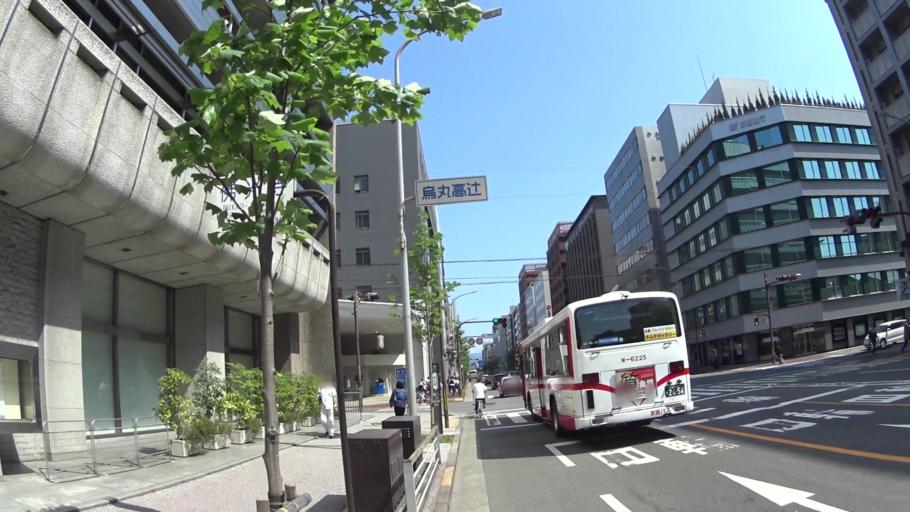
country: JP
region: Kyoto
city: Kyoto
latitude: 35.0000
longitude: 135.7597
